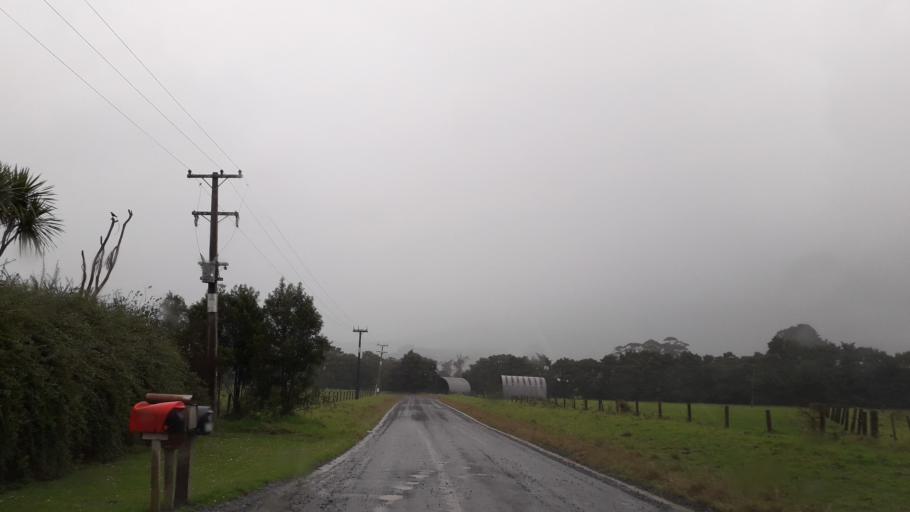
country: NZ
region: Northland
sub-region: Far North District
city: Waimate North
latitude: -35.5021
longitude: 173.6992
